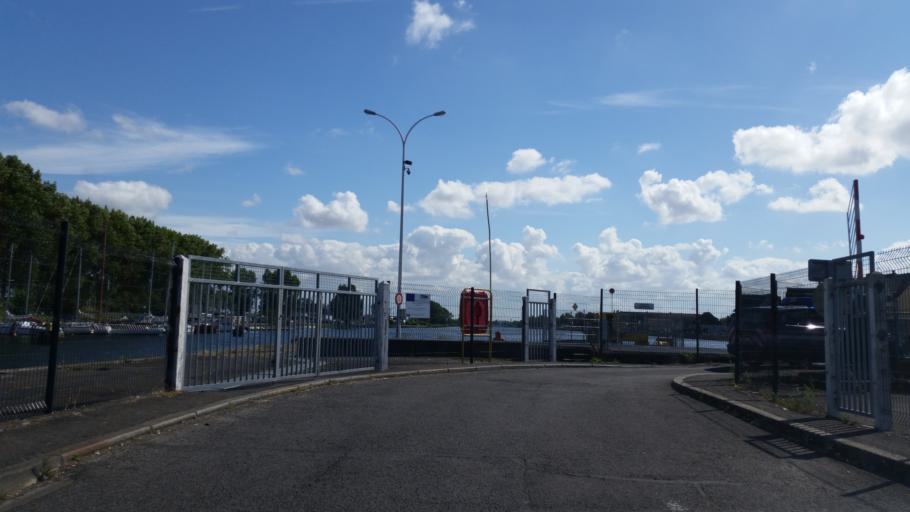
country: FR
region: Lower Normandy
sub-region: Departement du Calvados
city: Ouistreham
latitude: 49.2783
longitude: -0.2492
